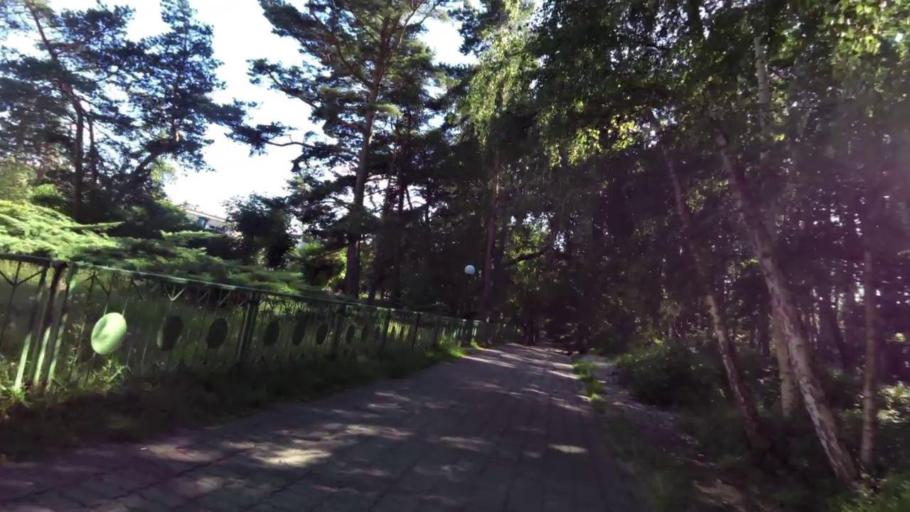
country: PL
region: West Pomeranian Voivodeship
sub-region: Powiat slawienski
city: Darlowo
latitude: 54.3789
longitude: 16.3114
